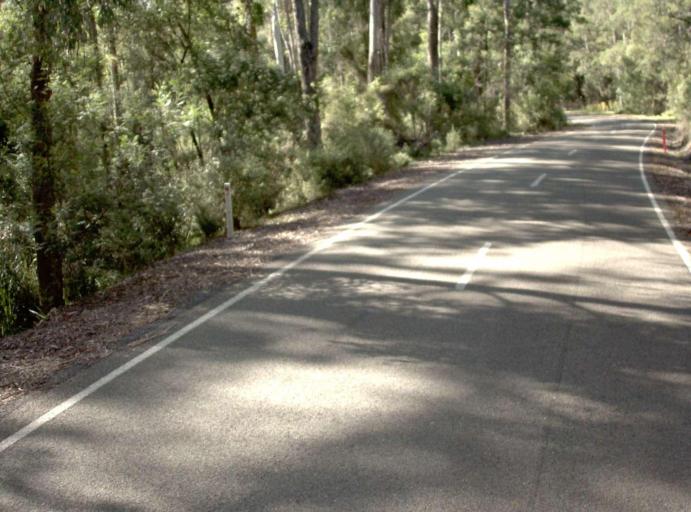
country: AU
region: Victoria
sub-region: East Gippsland
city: Lakes Entrance
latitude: -37.4892
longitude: 148.5542
